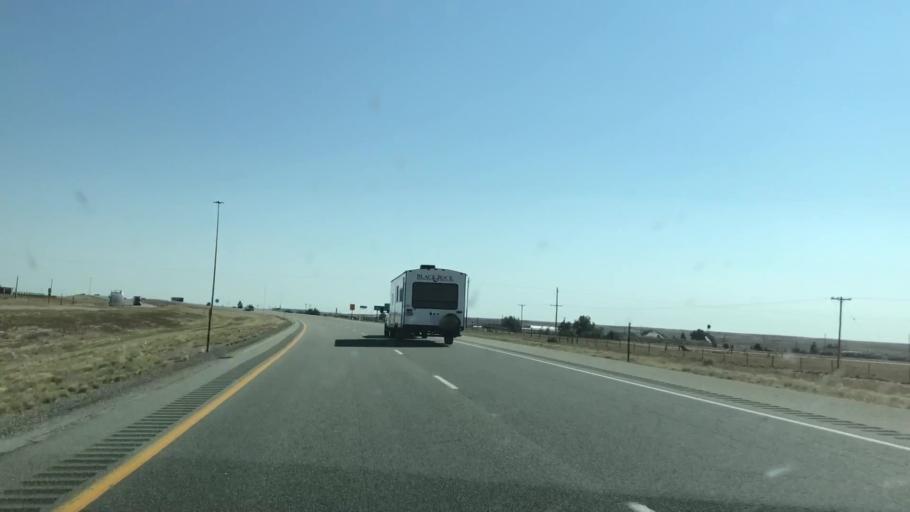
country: US
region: Wyoming
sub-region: Carbon County
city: Rawlins
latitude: 41.6709
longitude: -107.9902
